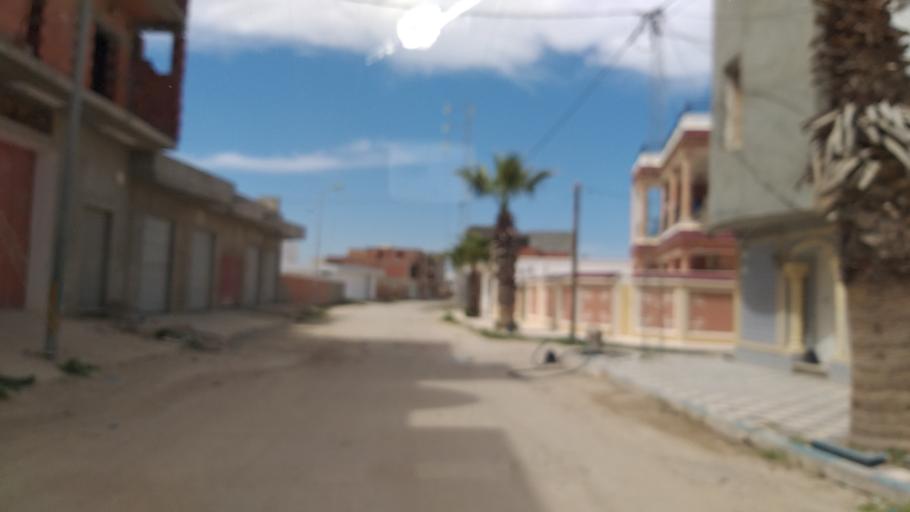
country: TN
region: Al Mahdiyah
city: El Jem
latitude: 35.3018
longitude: 10.6988
